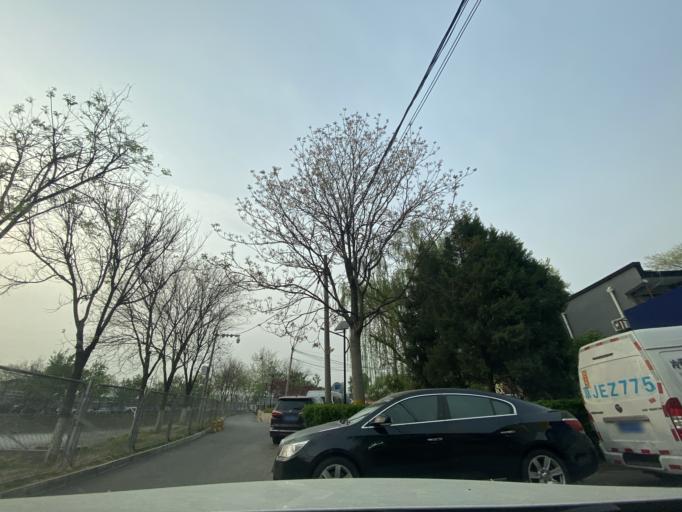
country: CN
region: Beijing
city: Sijiqing
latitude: 39.9301
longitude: 116.2646
